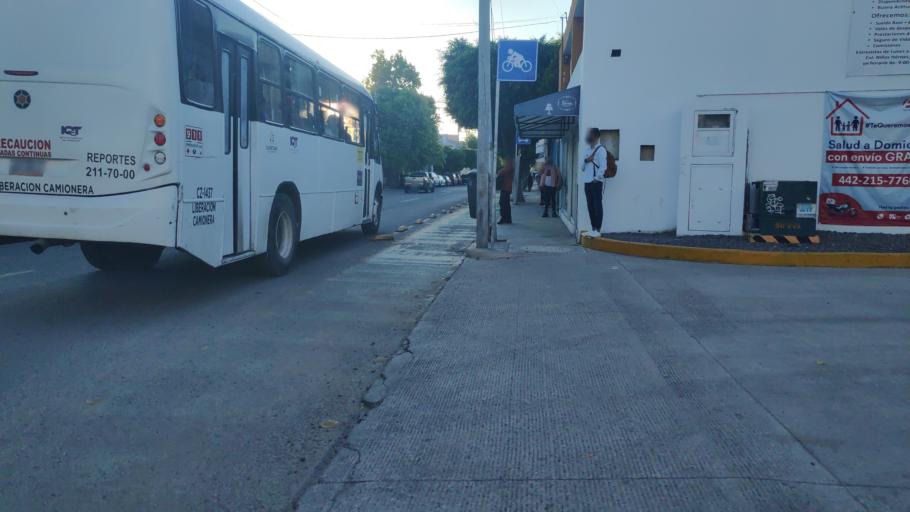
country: MX
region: Queretaro
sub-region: Queretaro
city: Santiago de Queretaro
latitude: 20.5926
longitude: -100.3782
